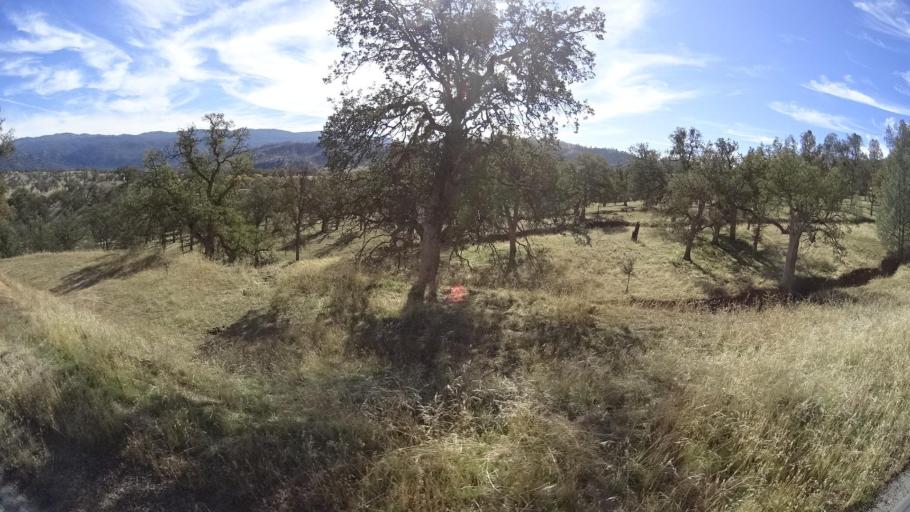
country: US
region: California
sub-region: Kern County
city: Alta Sierra
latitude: 35.6296
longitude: -118.7555
